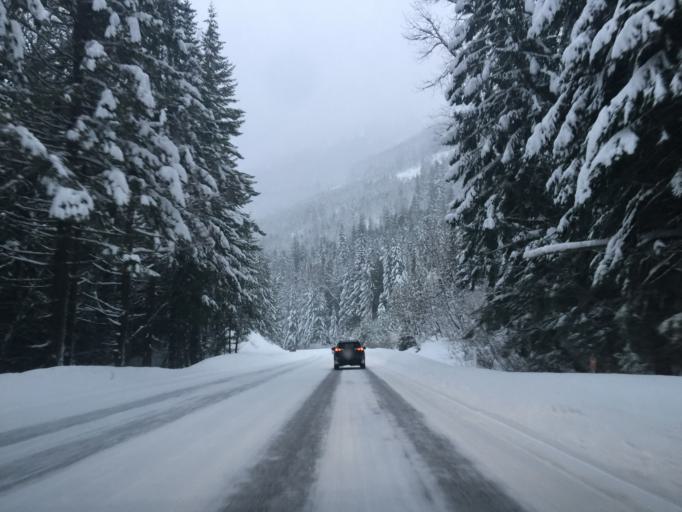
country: US
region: Washington
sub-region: Chelan County
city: Leavenworth
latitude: 47.7675
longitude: -120.9920
